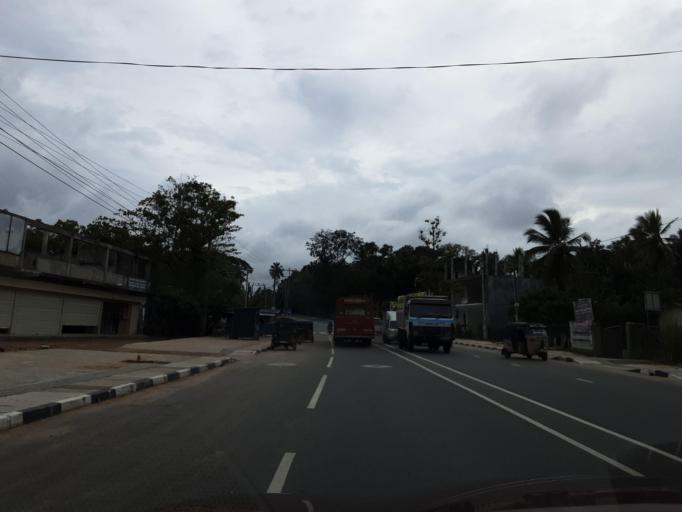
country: LK
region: Uva
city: Badulla
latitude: 7.3994
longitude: 81.2423
